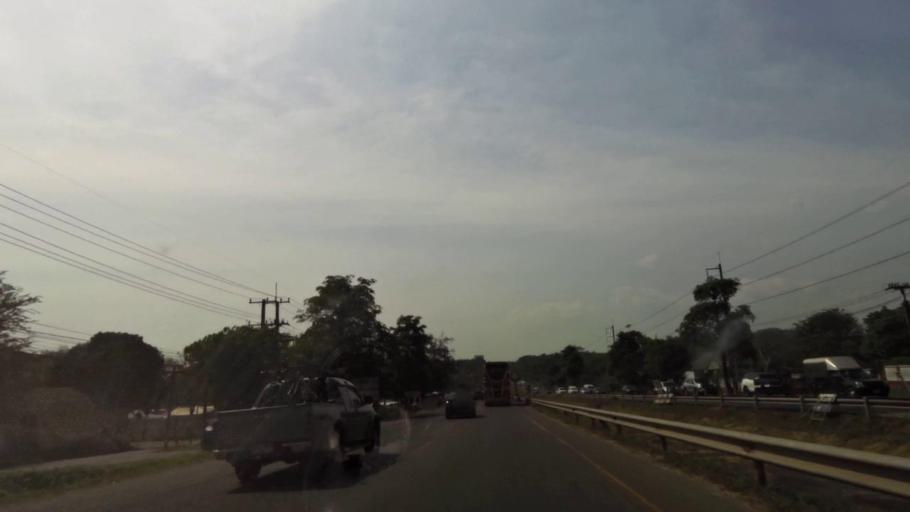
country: TH
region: Chanthaburi
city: Chanthaburi
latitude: 12.6656
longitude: 102.0899
